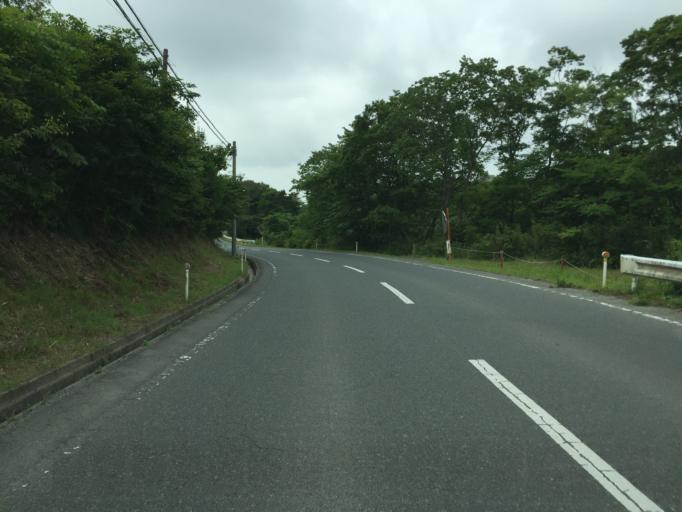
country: JP
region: Miyagi
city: Marumori
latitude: 37.7513
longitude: 140.9601
